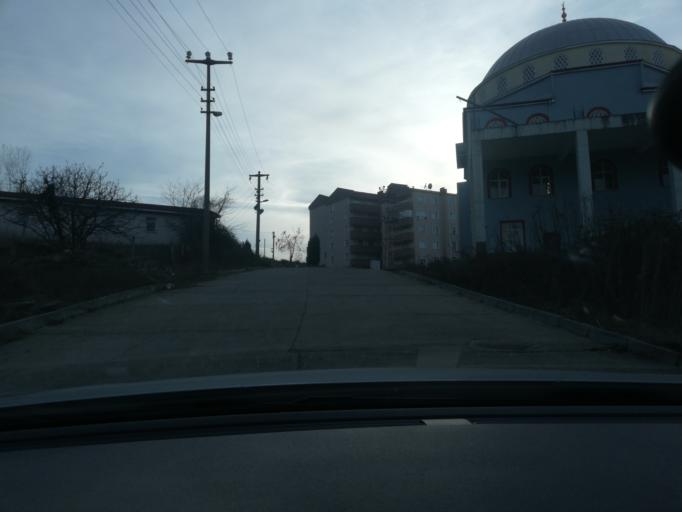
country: TR
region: Zonguldak
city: Tieum
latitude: 41.5580
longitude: 32.0282
